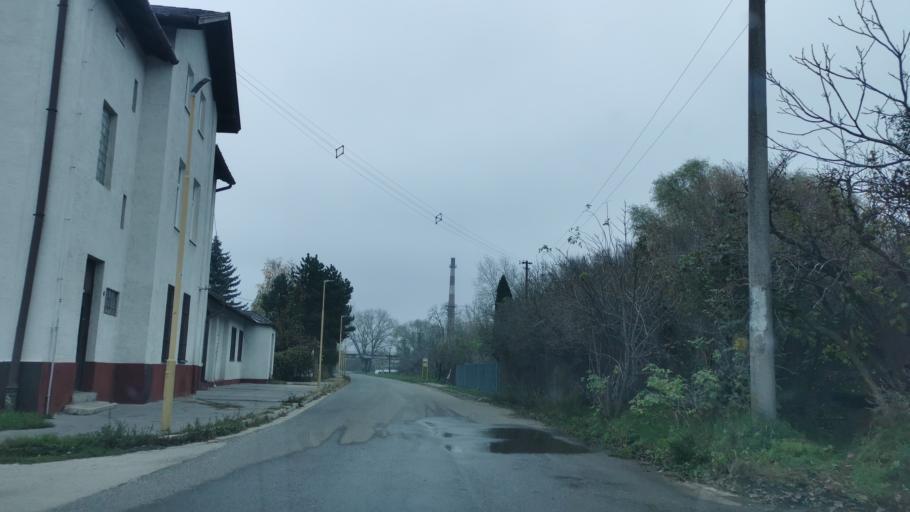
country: SK
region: Trnavsky
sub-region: Okres Skalica
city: Holic
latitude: 48.8143
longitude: 17.1502
